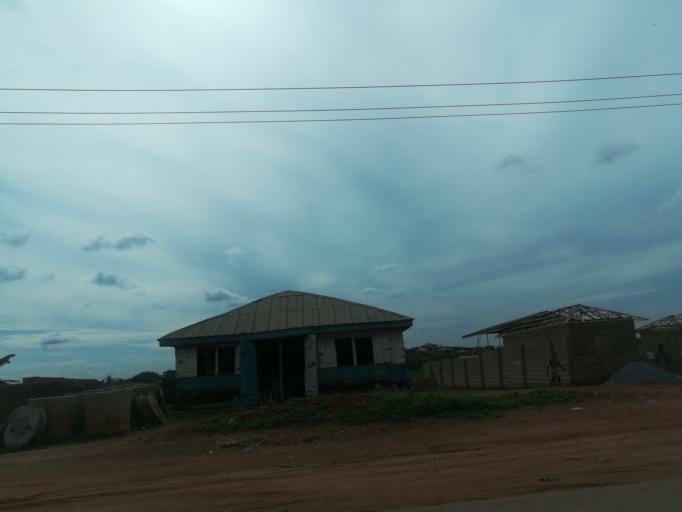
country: NG
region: Oyo
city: Ibadan
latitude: 7.3855
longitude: 3.9729
